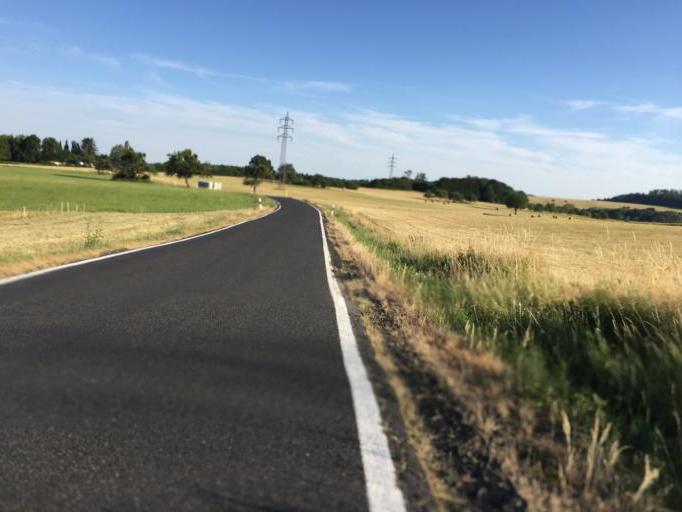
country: DE
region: Rheinland-Pfalz
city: Meudt
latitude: 50.5046
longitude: 7.8956
